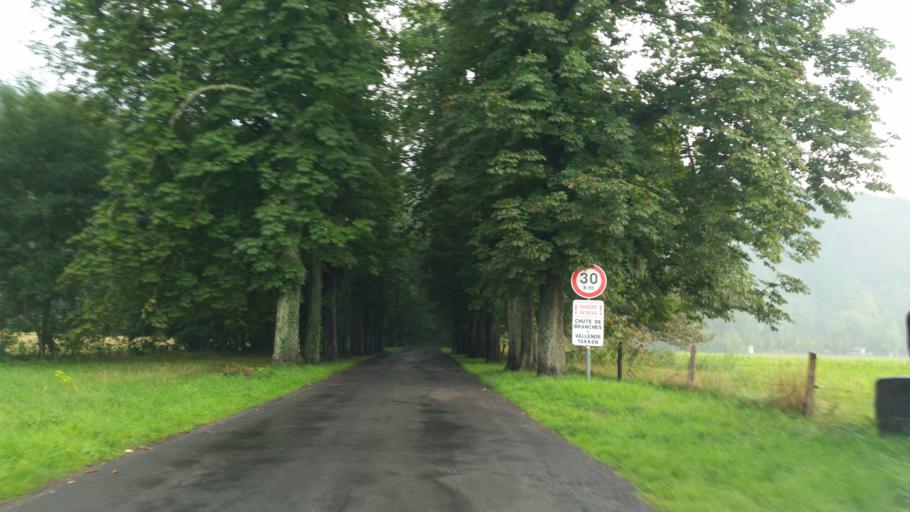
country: BE
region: Wallonia
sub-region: Province de Namur
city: Rochefort
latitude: 50.1237
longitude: 5.1944
